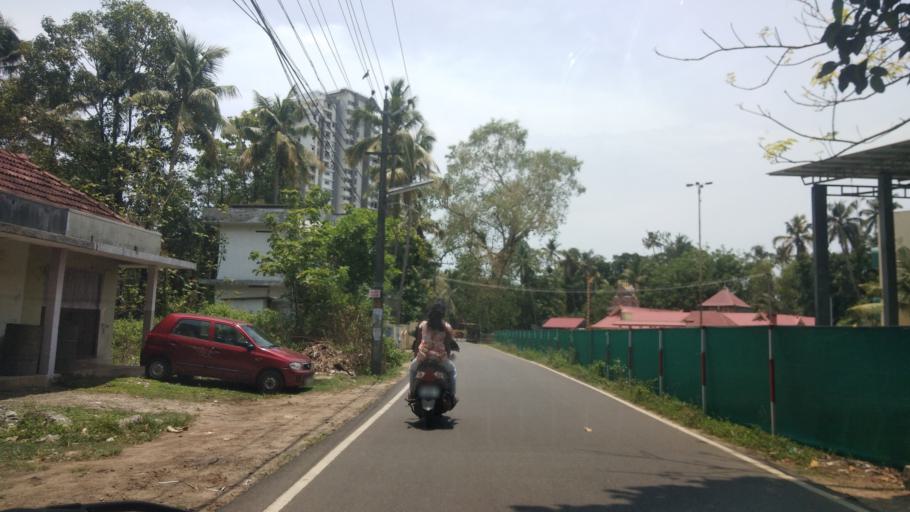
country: IN
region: Kerala
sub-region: Alappuzha
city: Arukutti
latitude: 9.8947
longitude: 76.3101
